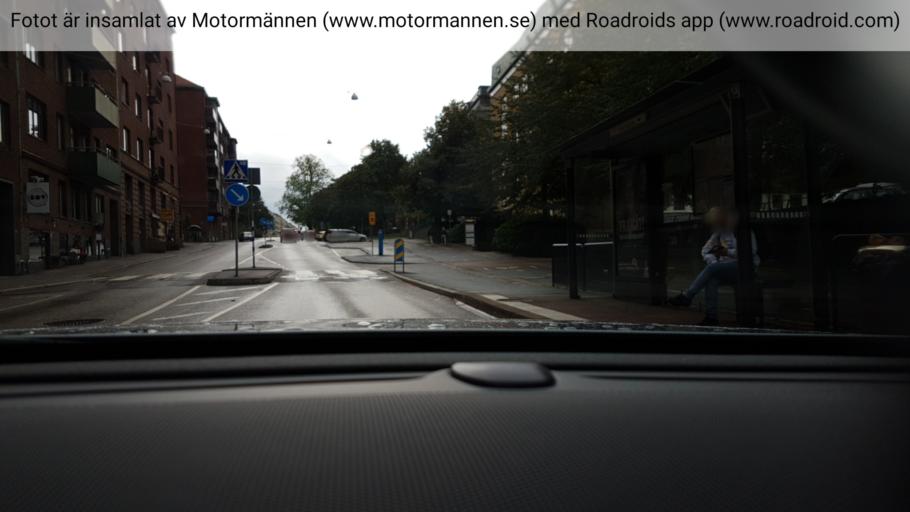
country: SE
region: Vaestra Goetaland
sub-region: Goteborg
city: Goeteborg
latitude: 57.6927
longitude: 11.9771
